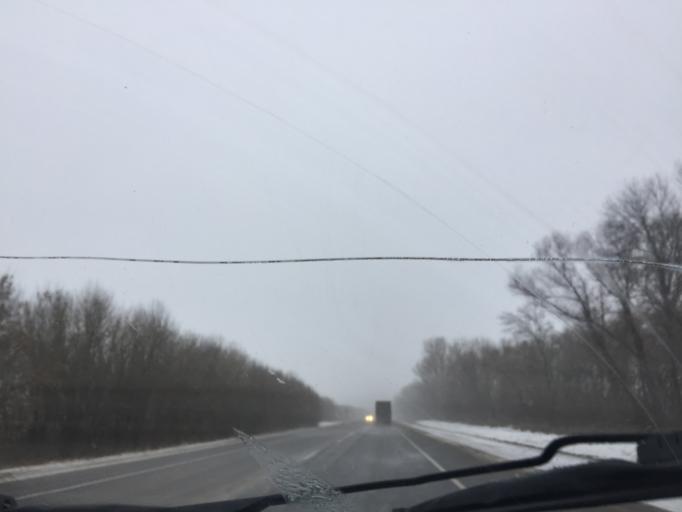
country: RU
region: Tula
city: Plavsk
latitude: 53.7758
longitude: 37.3538
